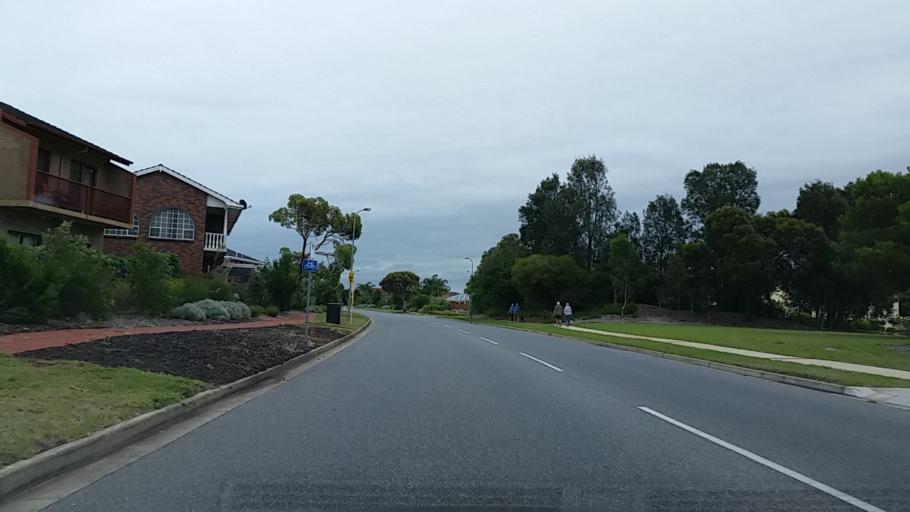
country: AU
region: South Australia
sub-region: Charles Sturt
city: West Lakes Shore
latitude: -34.8713
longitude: 138.4922
